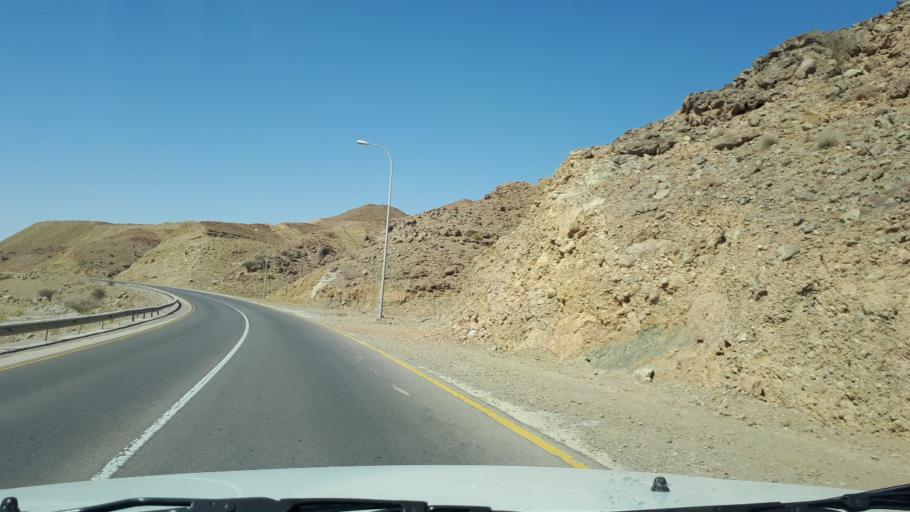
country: OM
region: Ash Sharqiyah
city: Sur
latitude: 22.3369
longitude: 59.3089
